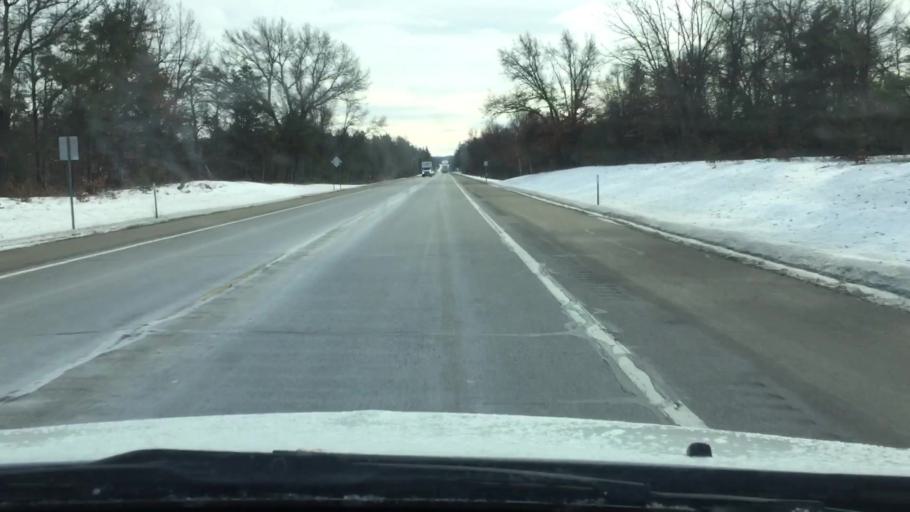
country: US
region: Michigan
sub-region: Wexford County
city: Manton
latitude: 44.5030
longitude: -85.4059
